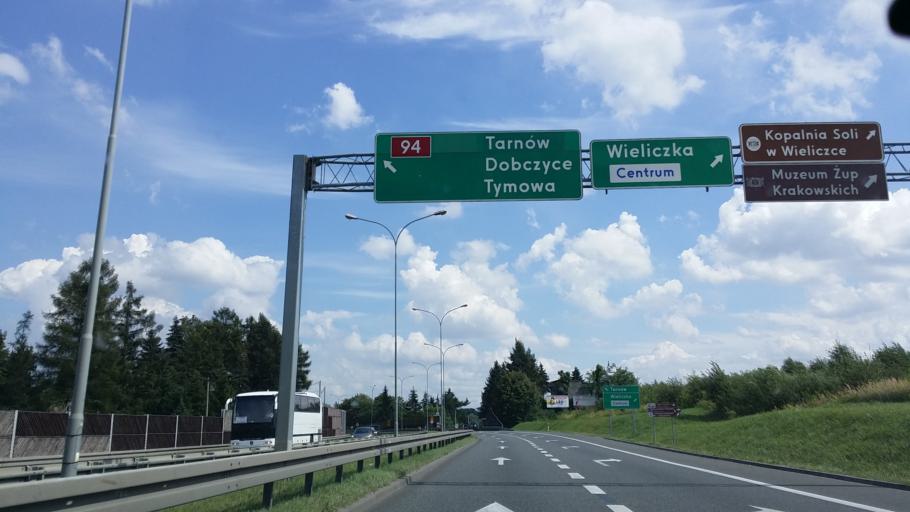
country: PL
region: Lesser Poland Voivodeship
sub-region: Powiat wielicki
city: Wieliczka
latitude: 49.9950
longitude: 20.0377
